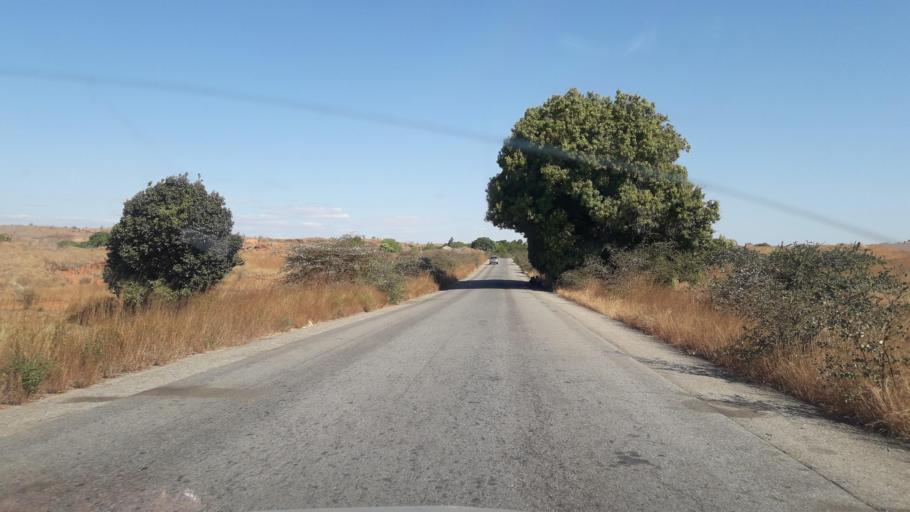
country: MG
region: Betsiboka
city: Maevatanana
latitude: -17.0285
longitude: 46.8057
